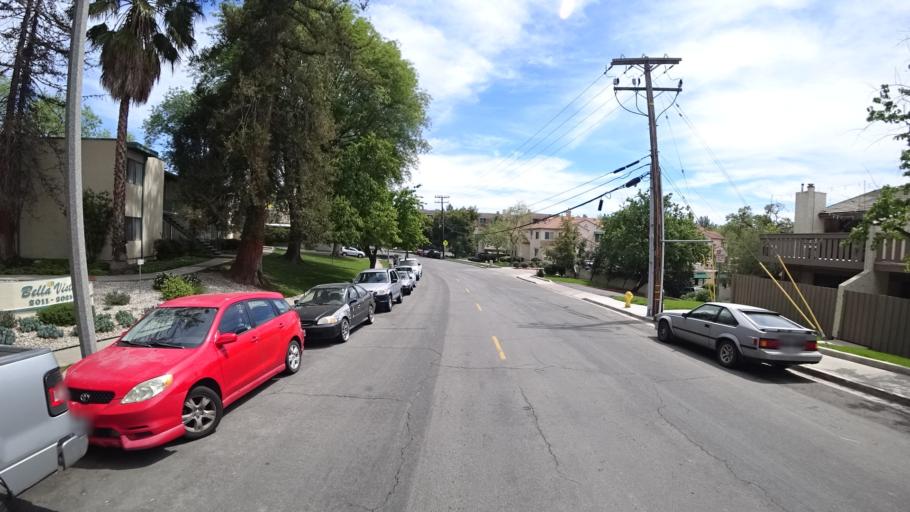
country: US
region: California
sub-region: Ventura County
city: Thousand Oaks
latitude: 34.1775
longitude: -118.8465
